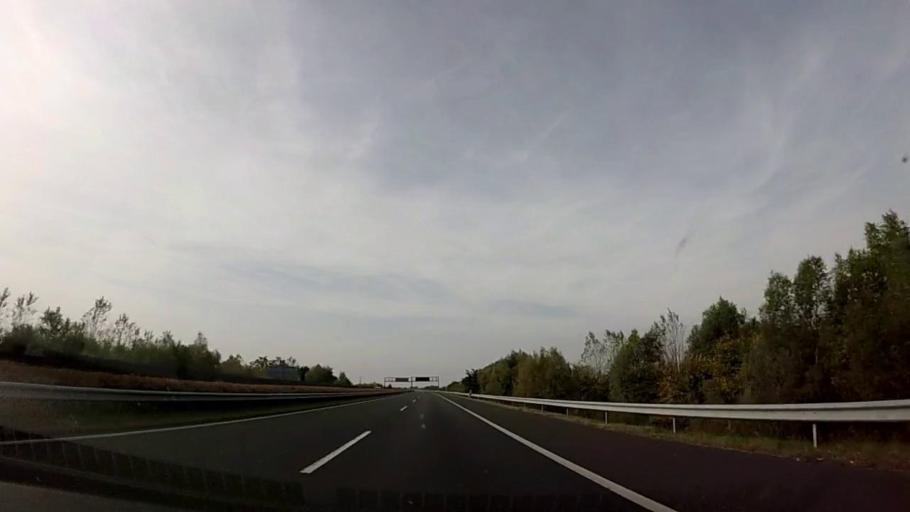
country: HU
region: Somogy
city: Balatonboglar
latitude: 46.7505
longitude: 17.6220
